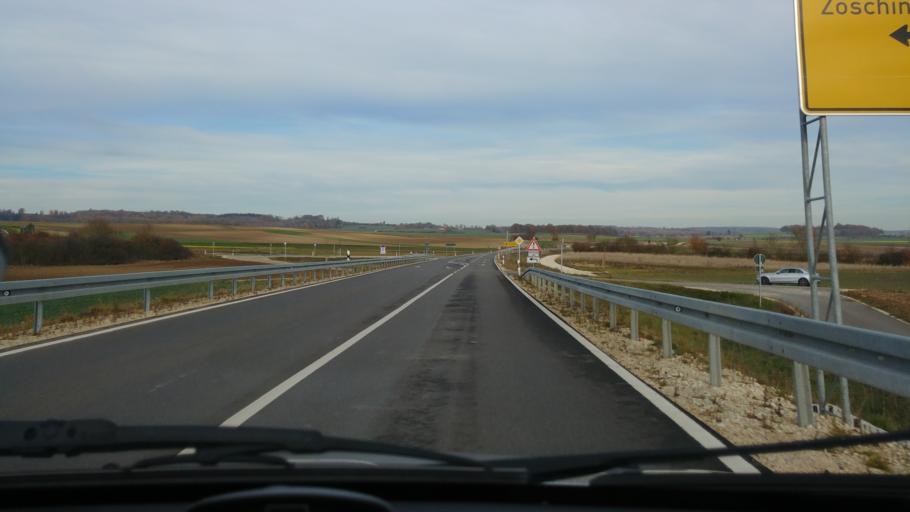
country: DE
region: Bavaria
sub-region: Swabia
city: Zoschingen
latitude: 48.6547
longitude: 10.3409
